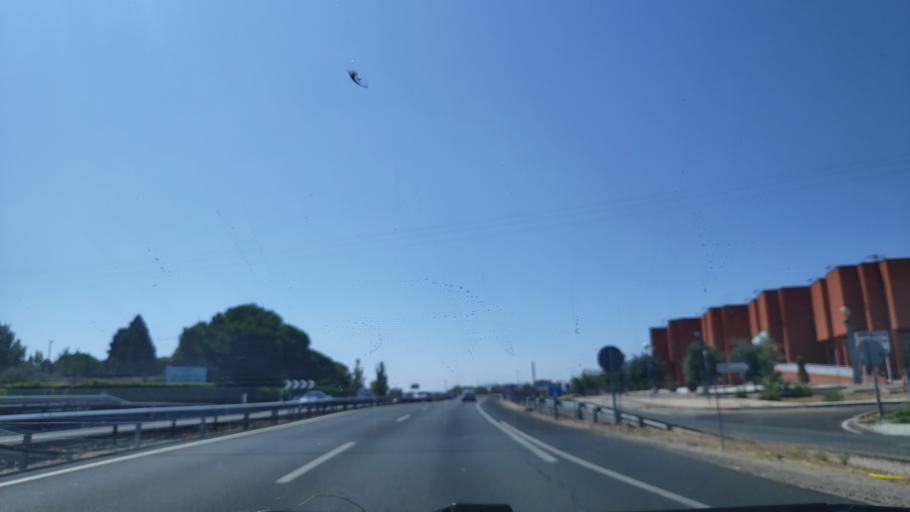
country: ES
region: Madrid
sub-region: Provincia de Madrid
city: Casarrubuelos
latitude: 40.1659
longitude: -3.8160
